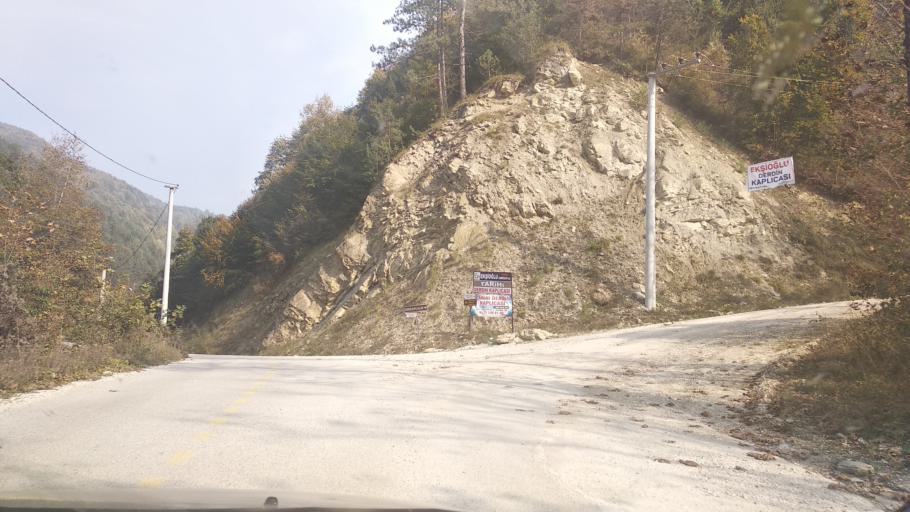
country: TR
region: Duzce
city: Kaynasli
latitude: 40.7254
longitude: 31.2404
